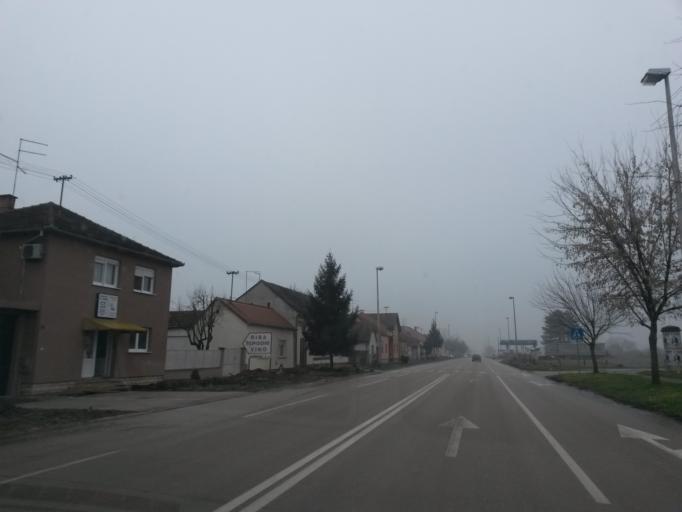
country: HR
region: Vukovarsko-Srijemska
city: Zupanja
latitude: 45.0814
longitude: 18.6956
